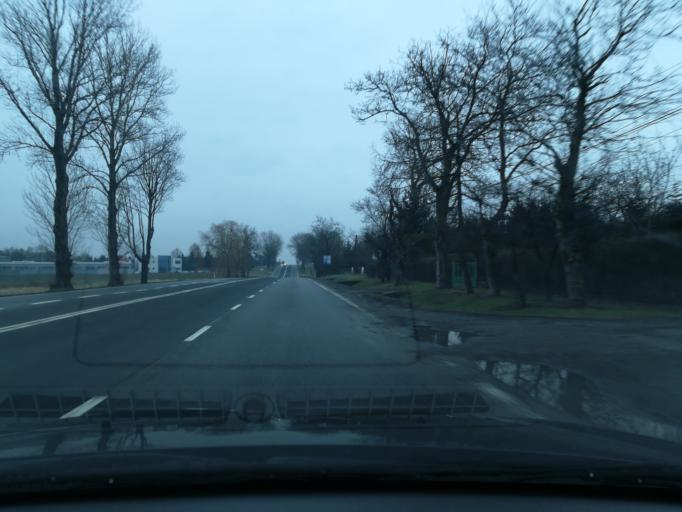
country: PL
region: Subcarpathian Voivodeship
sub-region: Powiat lancucki
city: Gluchow
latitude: 50.0803
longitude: 22.2785
